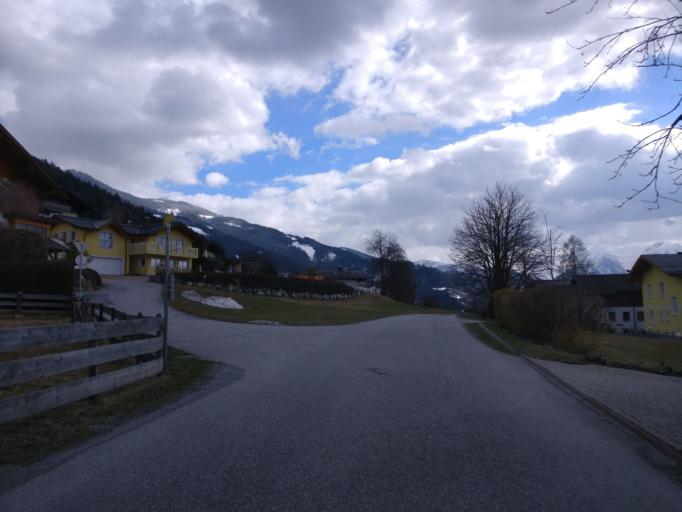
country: AT
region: Salzburg
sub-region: Politischer Bezirk Sankt Johann im Pongau
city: Bischofshofen
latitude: 47.4127
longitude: 13.2288
